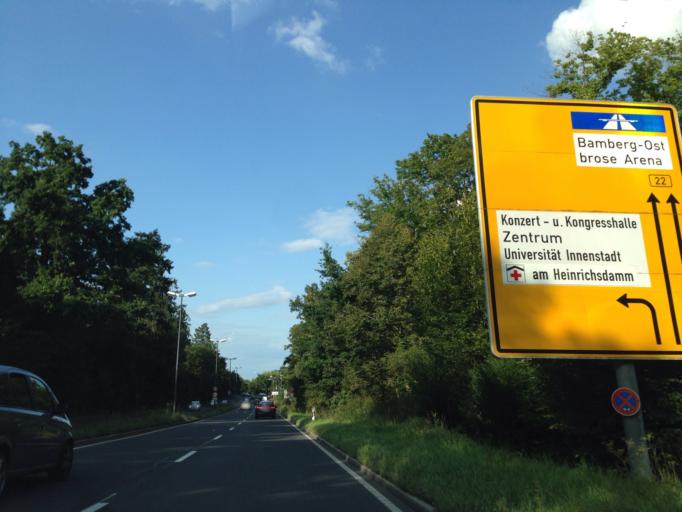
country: DE
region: Bavaria
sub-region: Upper Franconia
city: Bamberg
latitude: 49.8811
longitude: 10.9002
